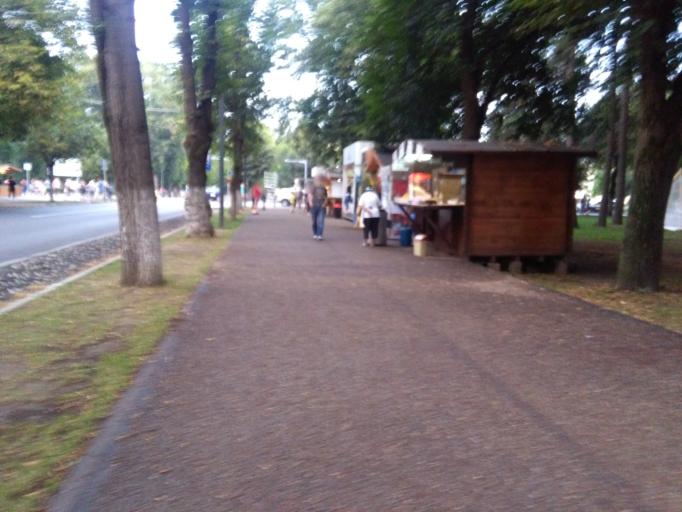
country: RO
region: Cluj
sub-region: Municipiul Cluj-Napoca
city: Cluj-Napoca
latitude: 46.7680
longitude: 23.5743
